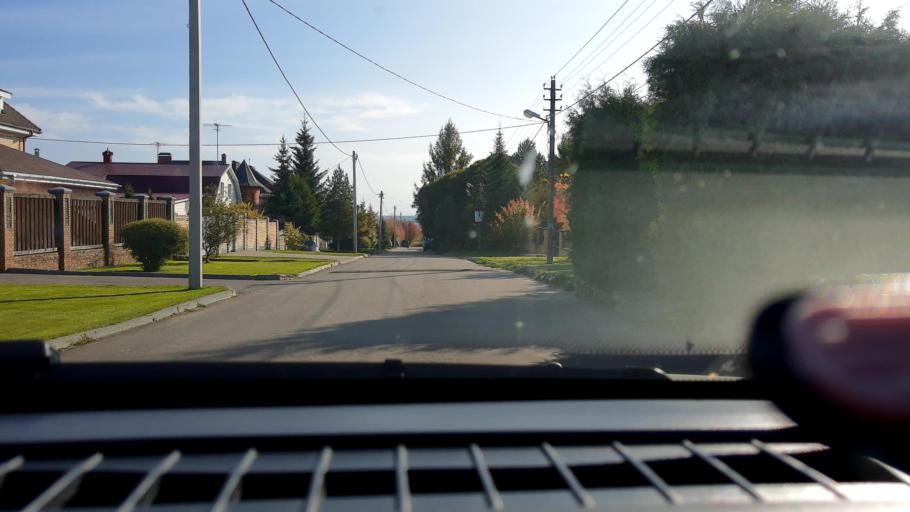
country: RU
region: Nizjnij Novgorod
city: Afonino
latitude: 56.2052
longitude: 43.9899
